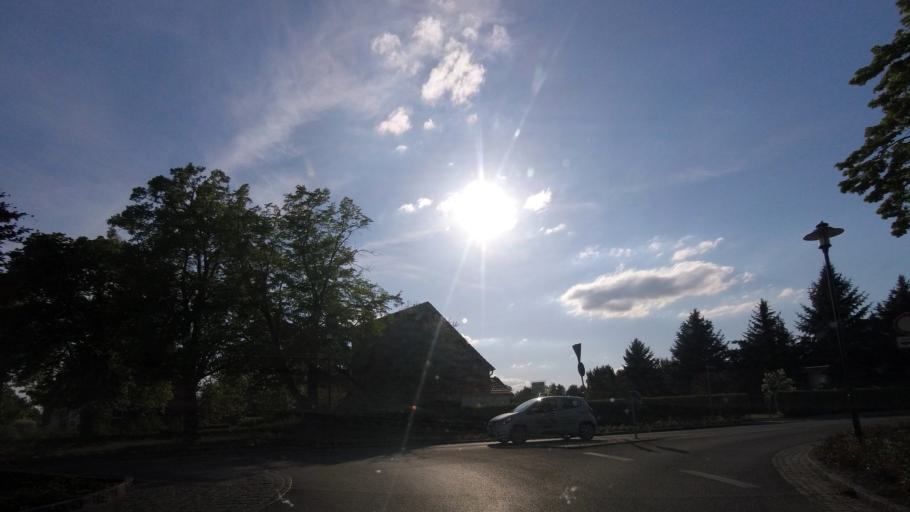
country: DE
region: Brandenburg
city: Lubbenau
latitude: 51.8658
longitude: 13.9652
